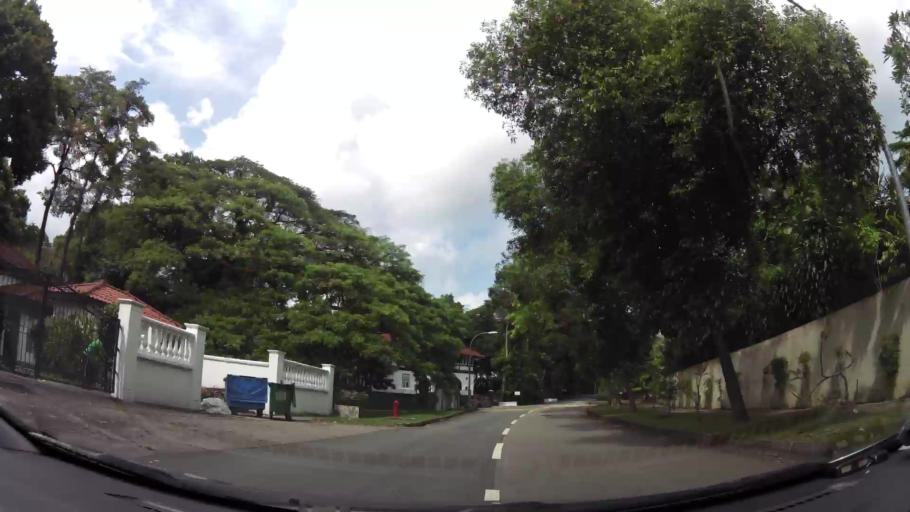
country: SG
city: Singapore
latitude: 1.3006
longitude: 103.8154
